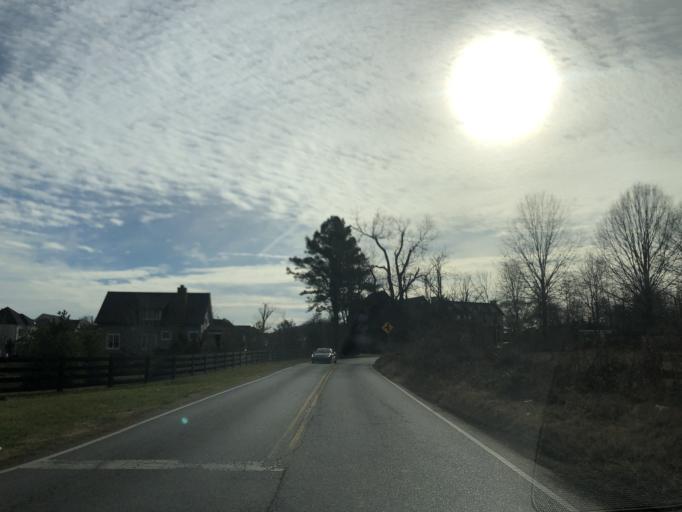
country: US
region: Tennessee
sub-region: Williamson County
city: Franklin
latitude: 35.9383
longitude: -86.9032
